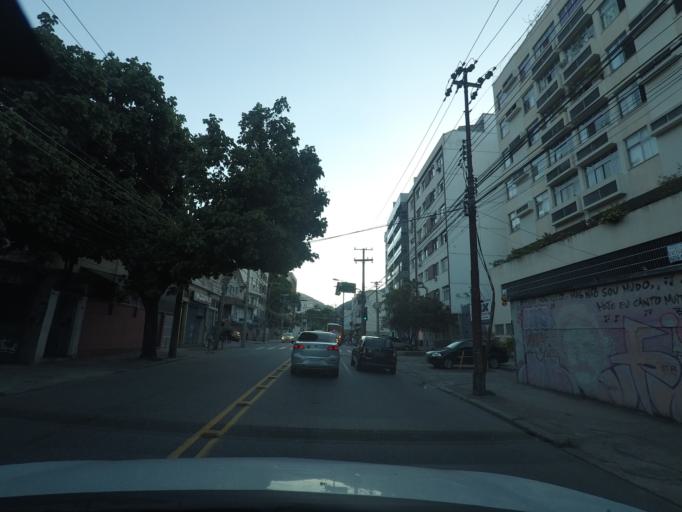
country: BR
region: Rio de Janeiro
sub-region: Rio De Janeiro
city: Rio de Janeiro
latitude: -22.9375
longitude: -43.2462
